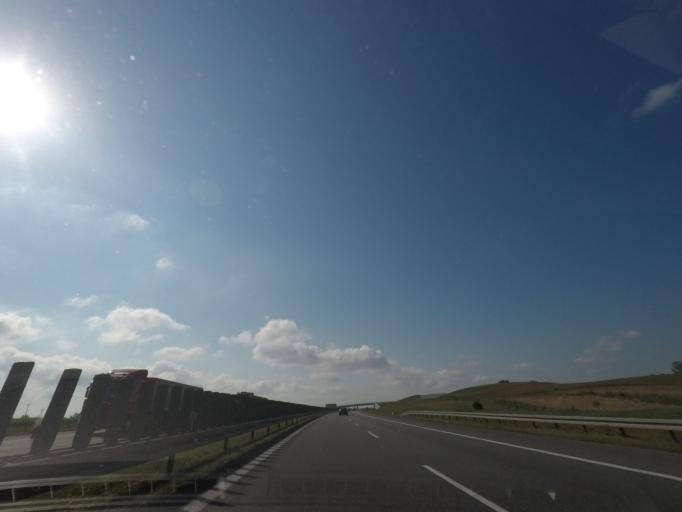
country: PL
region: Pomeranian Voivodeship
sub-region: Powiat gdanski
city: Pszczolki
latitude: 54.1747
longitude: 18.6510
